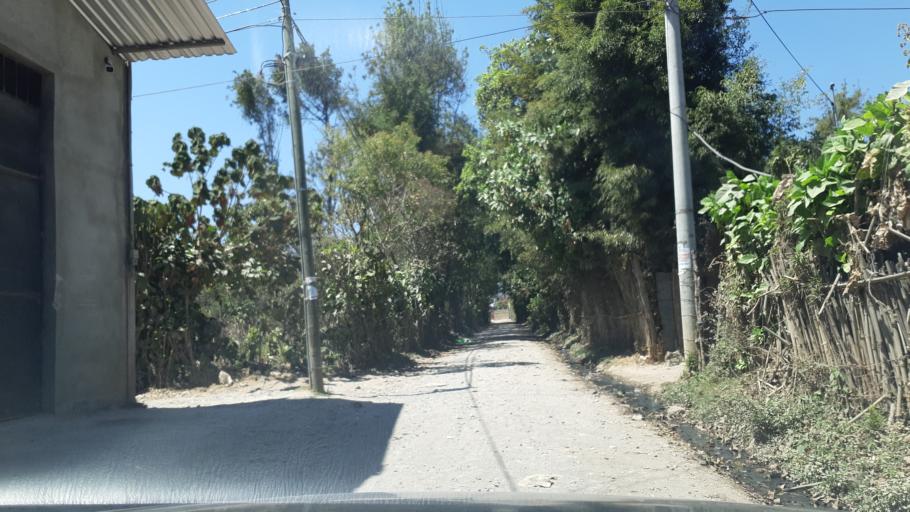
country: GT
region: Chimaltenango
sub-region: Municipio de Chimaltenango
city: Chimaltenango
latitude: 14.6526
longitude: -90.8095
